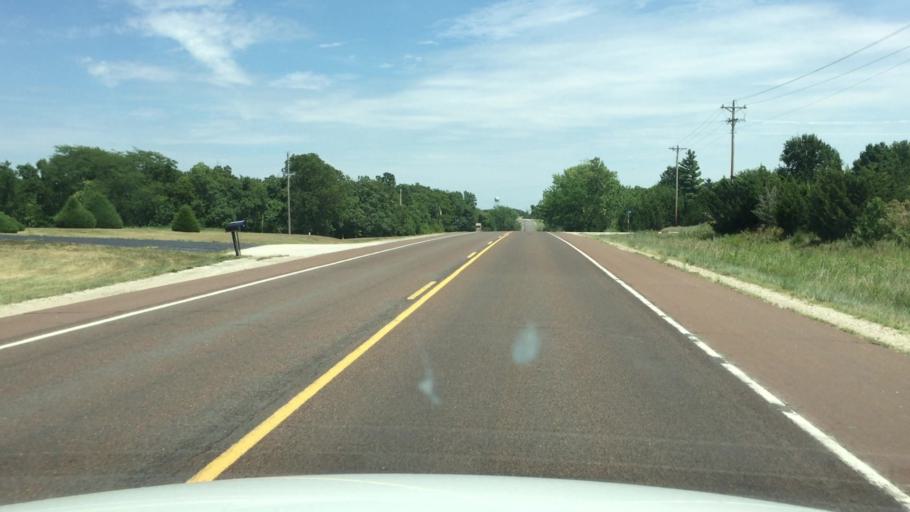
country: US
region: Kansas
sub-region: Douglas County
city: Lawrence
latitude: 38.9713
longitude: -95.3830
